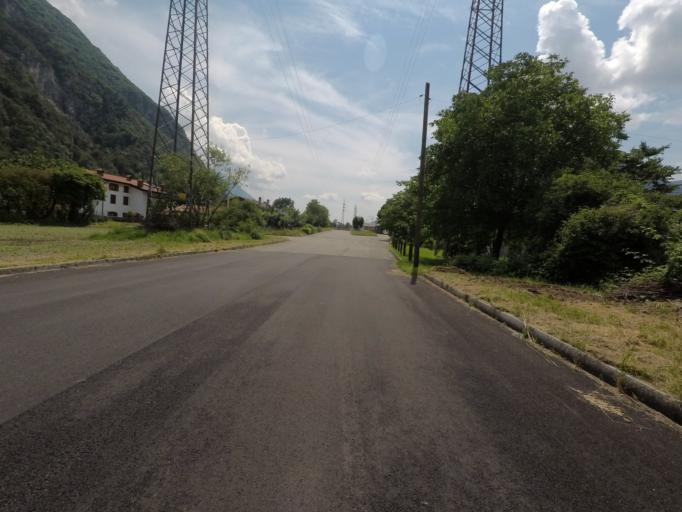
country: IT
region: Friuli Venezia Giulia
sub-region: Provincia di Udine
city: Amaro
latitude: 46.3753
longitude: 13.1338
